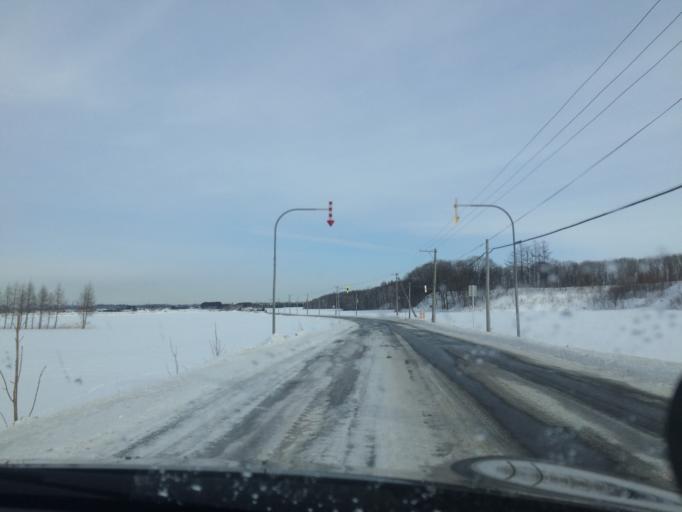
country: JP
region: Hokkaido
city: Obihiro
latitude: 42.9025
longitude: 143.0128
